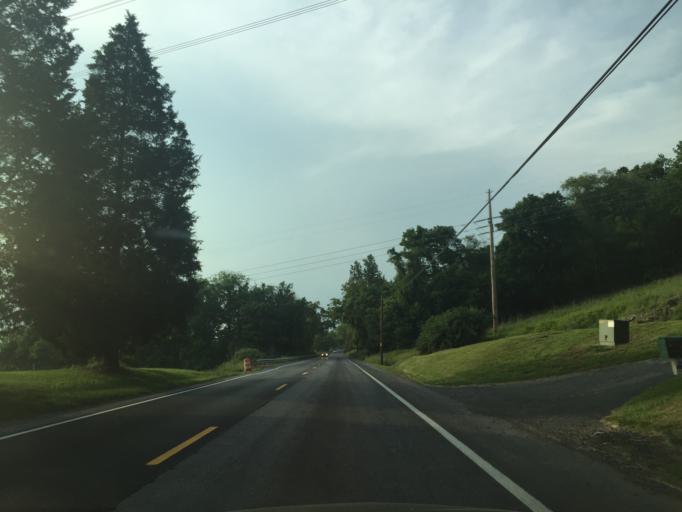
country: US
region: Maryland
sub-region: Frederick County
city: Point of Rocks
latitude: 39.2988
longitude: -77.5409
